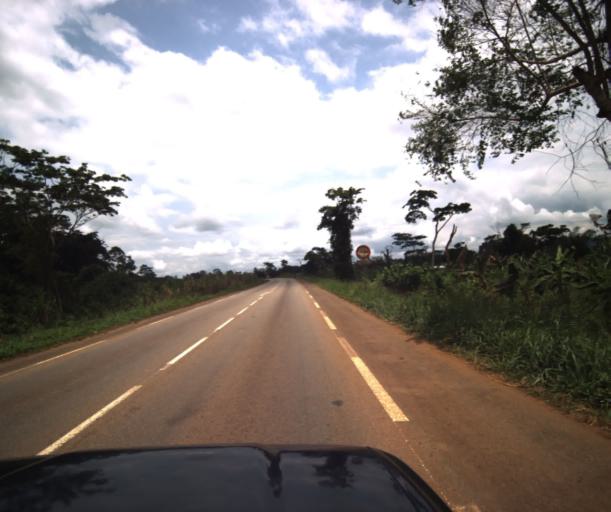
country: CM
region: Centre
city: Eseka
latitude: 3.8580
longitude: 10.9366
